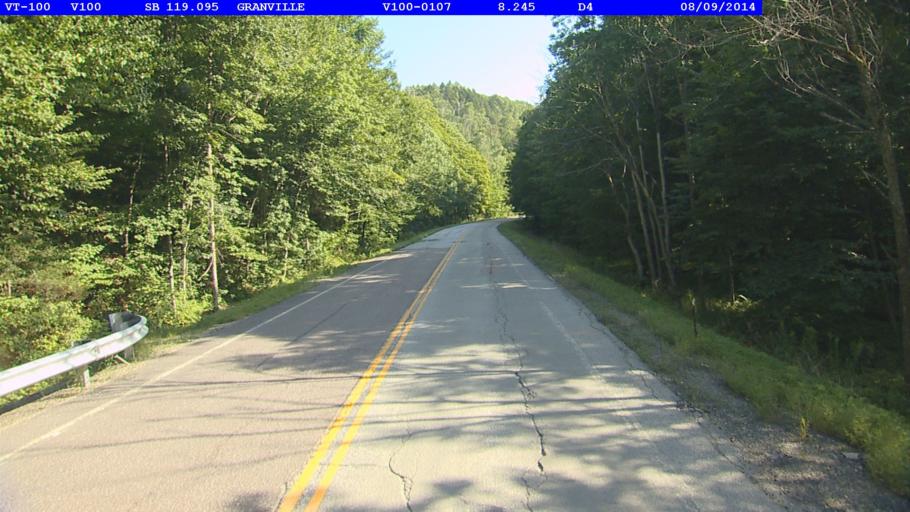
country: US
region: Vermont
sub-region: Washington County
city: Northfield
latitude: 44.0485
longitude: -72.8300
